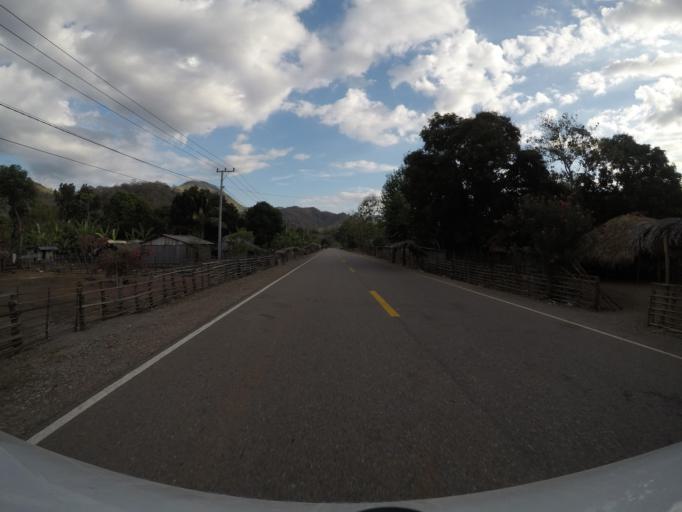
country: TL
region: Bobonaro
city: Maliana
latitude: -8.8641
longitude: 125.0468
